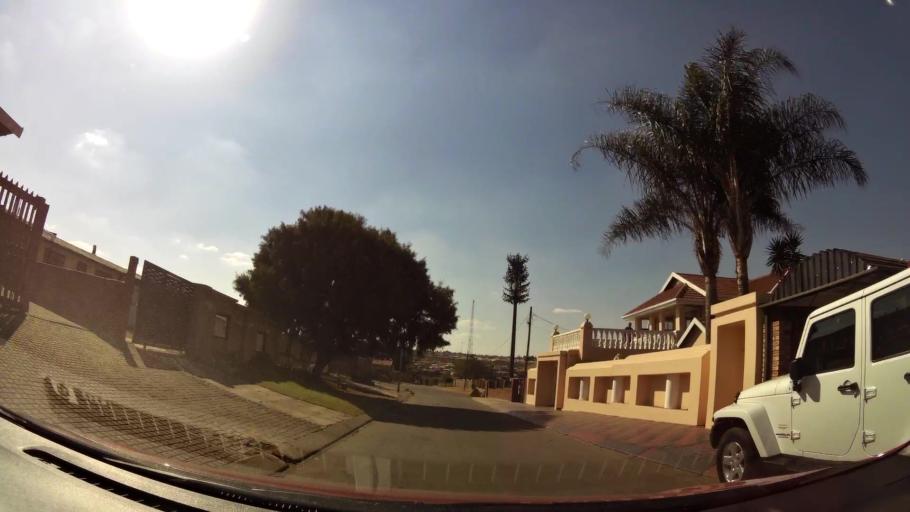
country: ZA
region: Gauteng
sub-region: City of Johannesburg Metropolitan Municipality
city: Soweto
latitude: -26.2329
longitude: 27.8839
